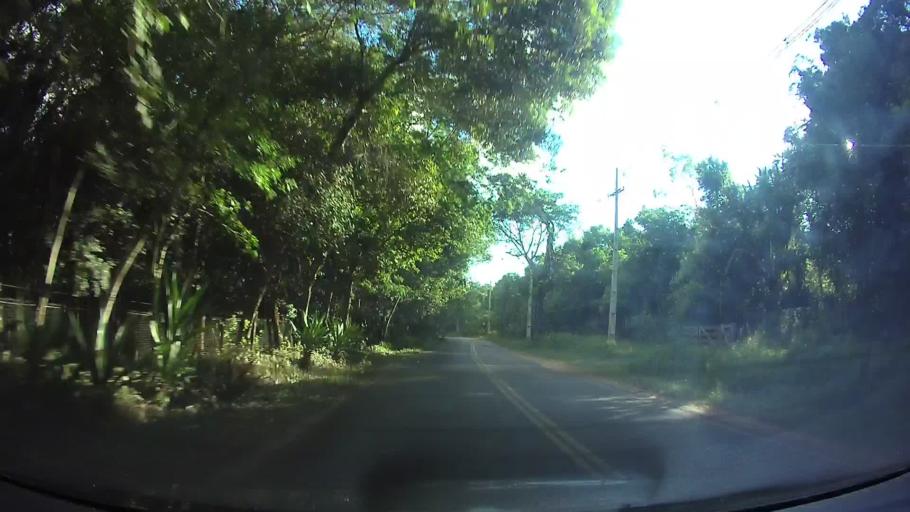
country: PY
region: Cordillera
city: Altos
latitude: -25.2317
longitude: -57.2290
